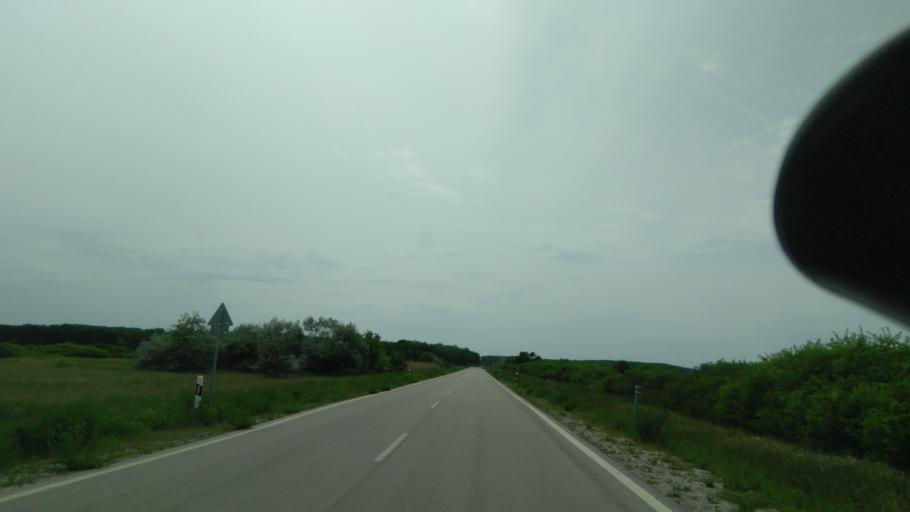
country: HU
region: Bekes
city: Mehkerek
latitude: 46.8633
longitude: 21.4604
